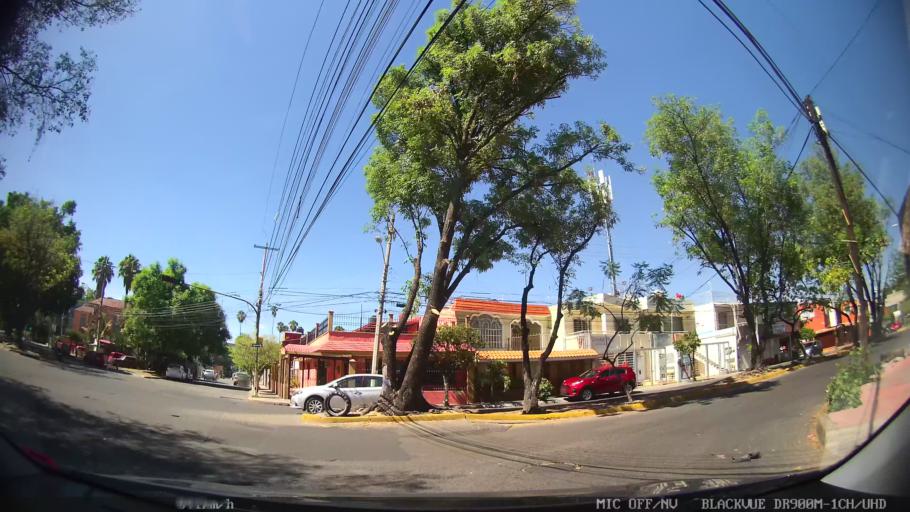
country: MX
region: Jalisco
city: Tlaquepaque
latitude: 20.6495
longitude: -103.3007
